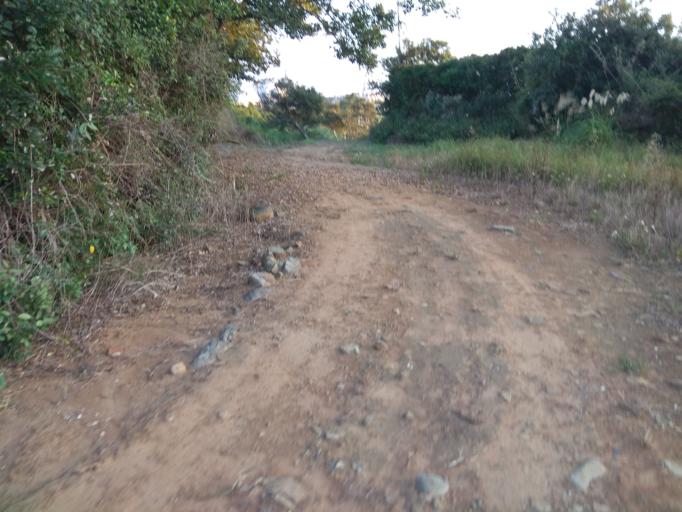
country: TW
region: Taiwan
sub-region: Hsinchu
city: Zhubei
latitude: 24.9875
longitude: 121.0363
